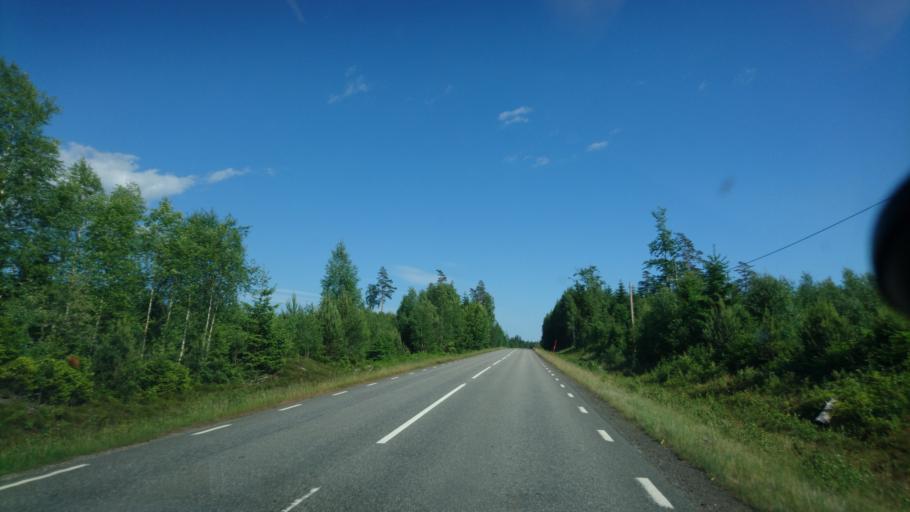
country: SE
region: Skane
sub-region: Osby Kommun
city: Lonsboda
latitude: 56.4265
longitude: 14.2745
